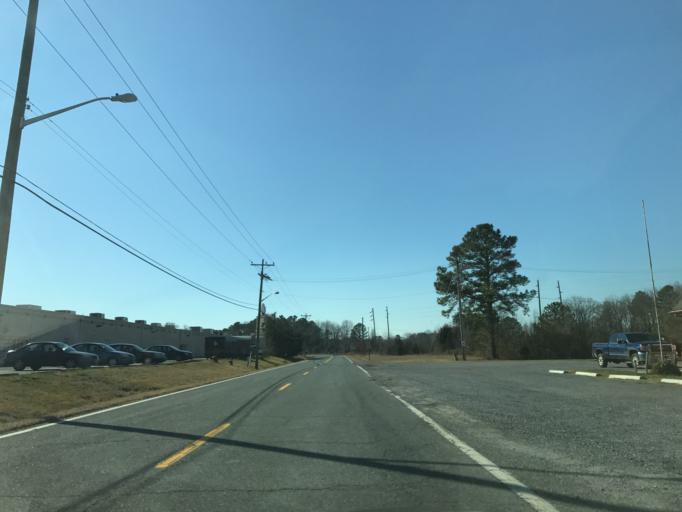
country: US
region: Maryland
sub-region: Queen Anne's County
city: Grasonville
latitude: 38.9845
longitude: -76.1579
